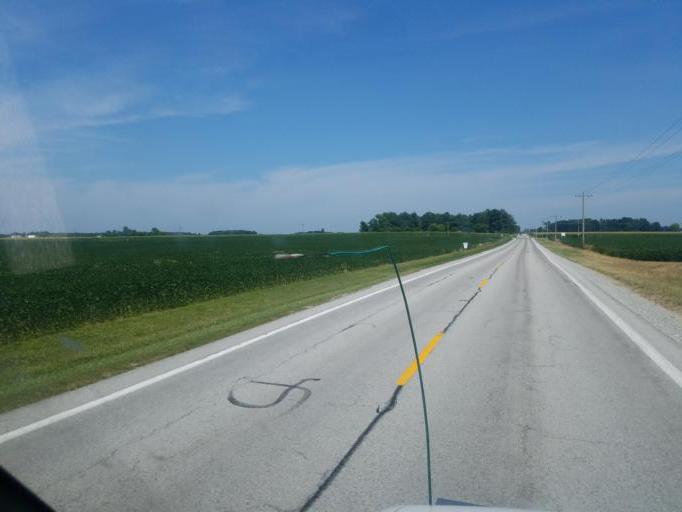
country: US
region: Ohio
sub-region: Shelby County
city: Botkins
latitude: 40.4964
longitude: -84.2627
